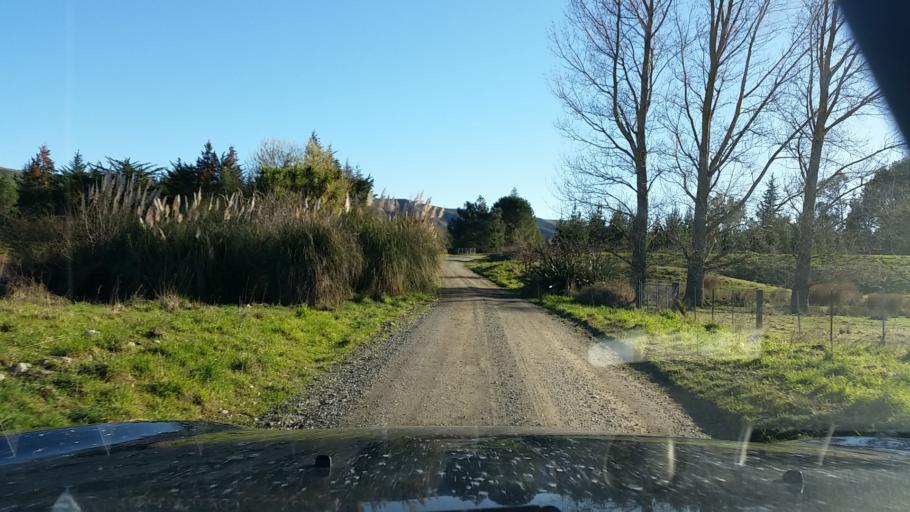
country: NZ
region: Marlborough
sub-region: Marlborough District
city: Blenheim
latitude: -41.6211
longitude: 173.6845
